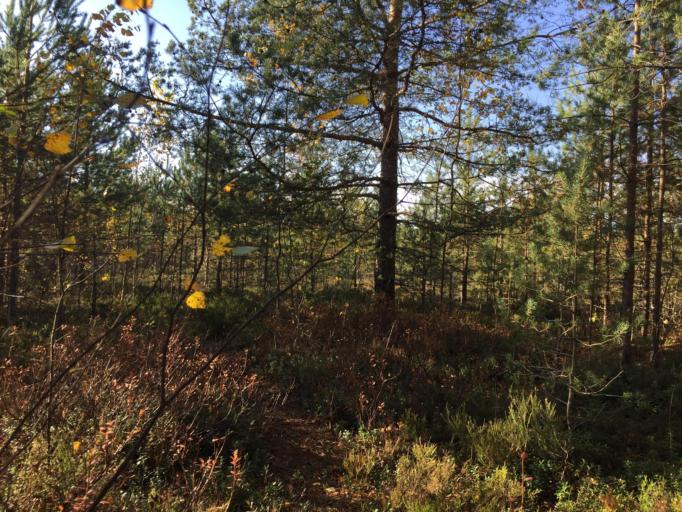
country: RU
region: Leningrad
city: Siverskiy
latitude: 59.3178
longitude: 30.0312
